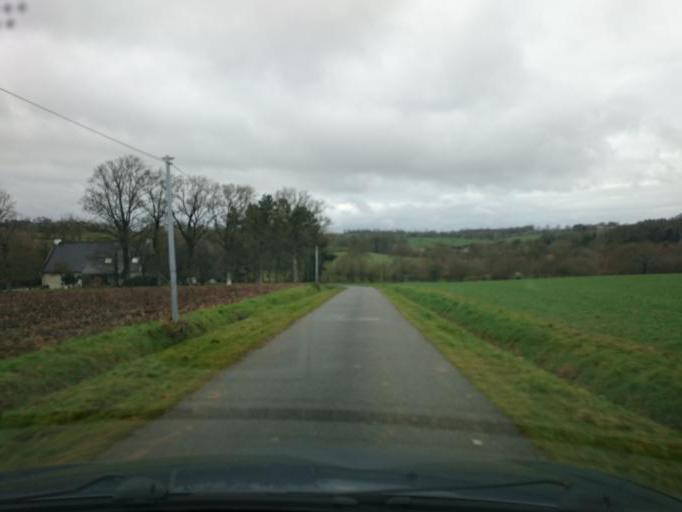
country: FR
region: Brittany
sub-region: Departement d'Ille-et-Vilaine
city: Chanteloup
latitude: 47.9357
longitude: -1.6012
